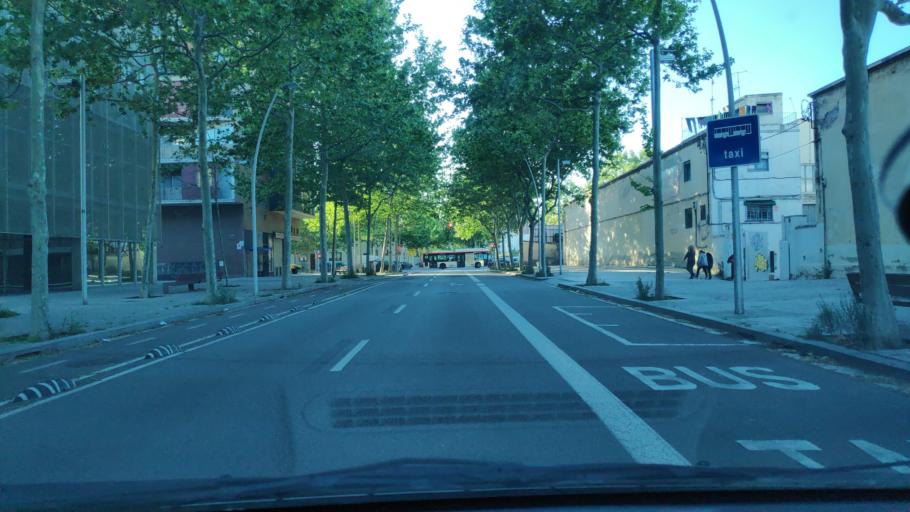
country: ES
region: Catalonia
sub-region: Provincia de Barcelona
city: Sant Marti
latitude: 41.4128
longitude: 2.2106
